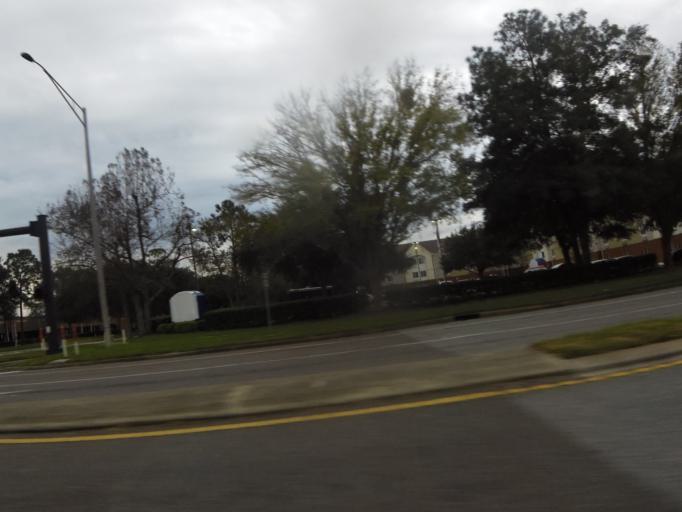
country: US
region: Florida
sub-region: Duval County
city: Jacksonville
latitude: 30.2472
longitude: -81.5842
